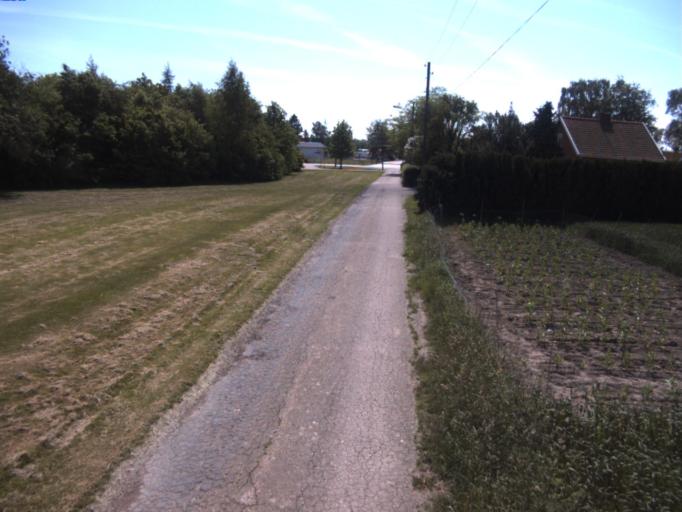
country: SE
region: Skane
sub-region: Helsingborg
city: Barslov
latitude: 56.0269
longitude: 12.8039
